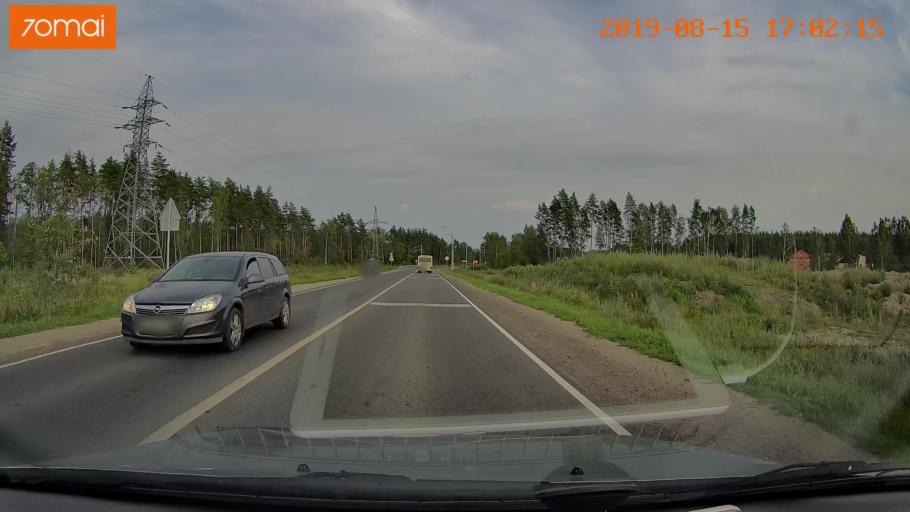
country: RU
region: Moskovskaya
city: Malyshevo
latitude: 55.4867
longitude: 38.3886
